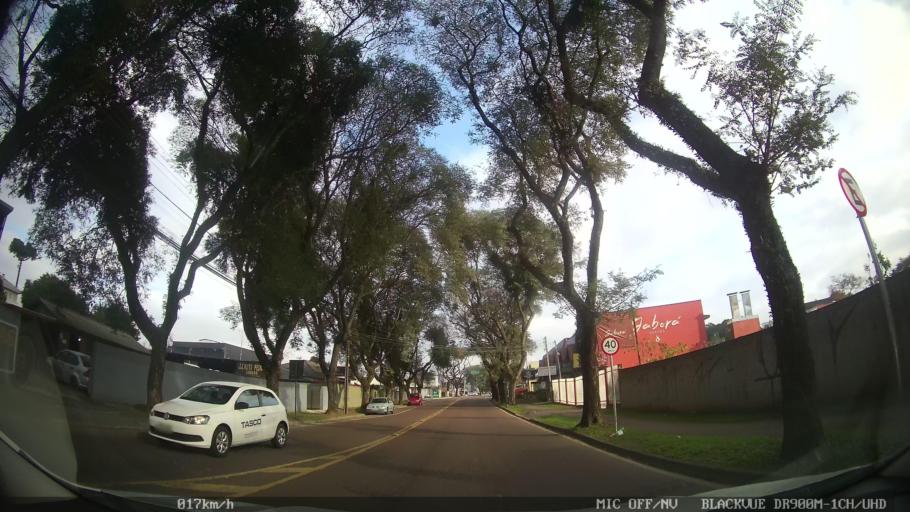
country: BR
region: Parana
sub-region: Curitiba
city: Curitiba
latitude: -25.4000
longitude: -49.3326
